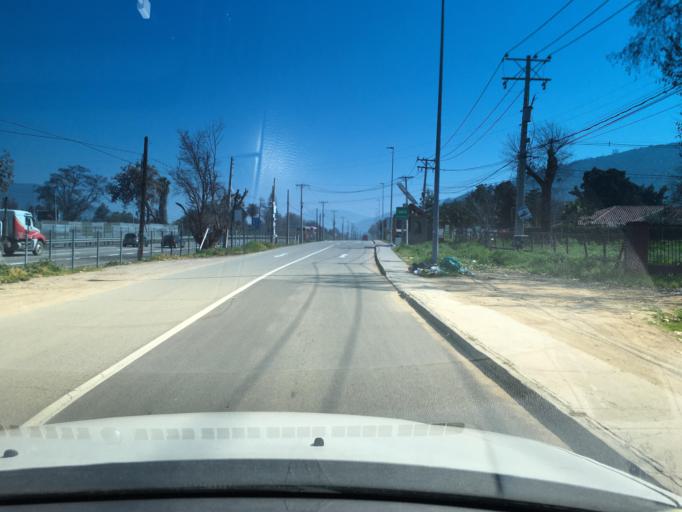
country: CL
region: Santiago Metropolitan
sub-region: Provincia de Chacabuco
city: Lampa
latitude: -33.4097
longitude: -71.0633
